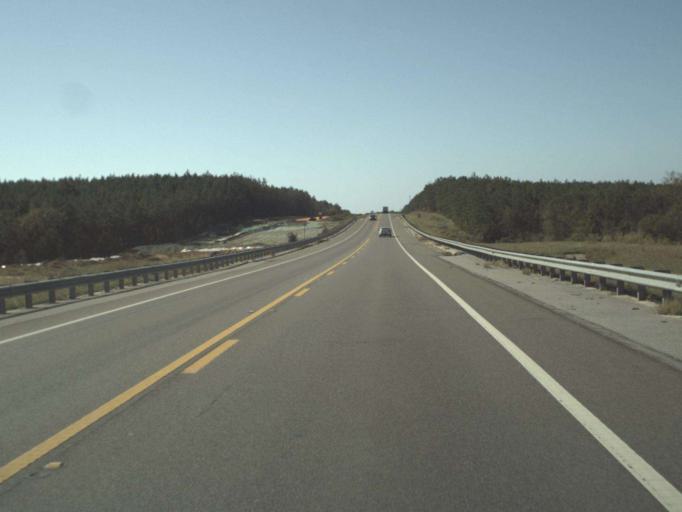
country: US
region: Florida
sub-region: Walton County
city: Freeport
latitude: 30.5122
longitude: -86.1123
